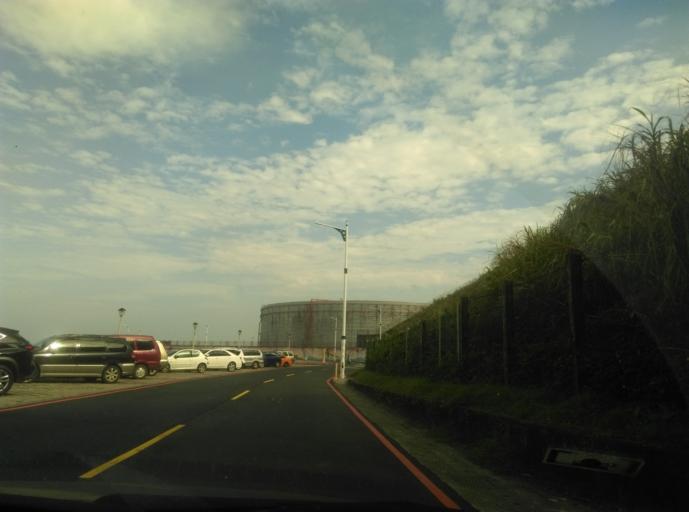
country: TW
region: Taiwan
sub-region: Keelung
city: Keelung
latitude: 25.1630
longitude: 121.7279
